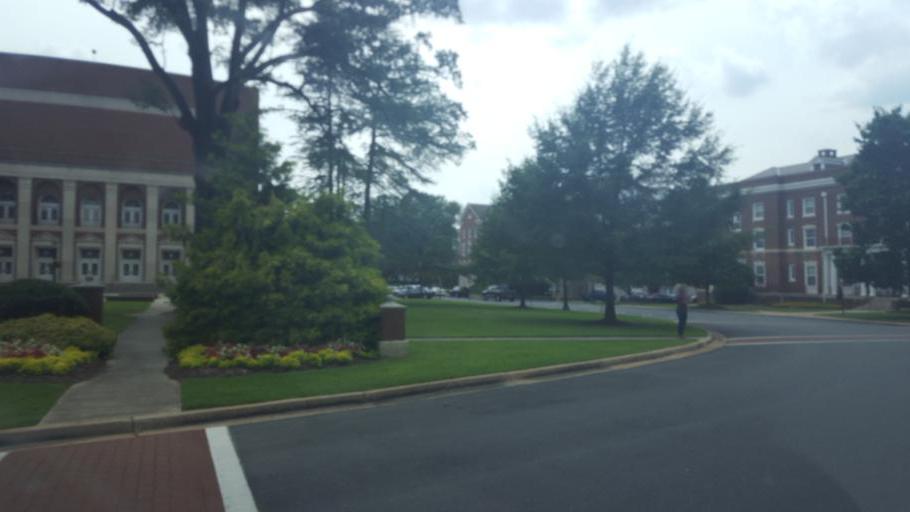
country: US
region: South Carolina
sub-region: York County
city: Rock Hill
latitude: 34.9411
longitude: -81.0308
